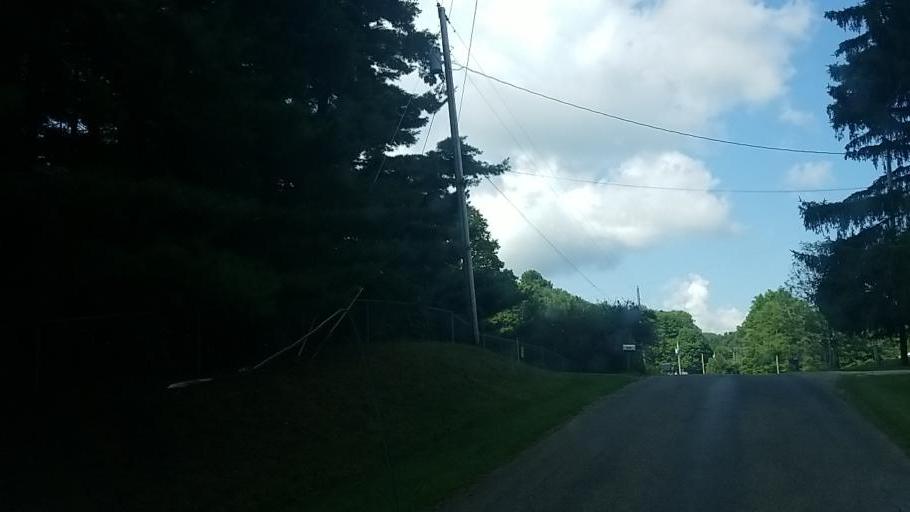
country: US
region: Ohio
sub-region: Ashland County
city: Loudonville
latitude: 40.7407
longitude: -82.3049
